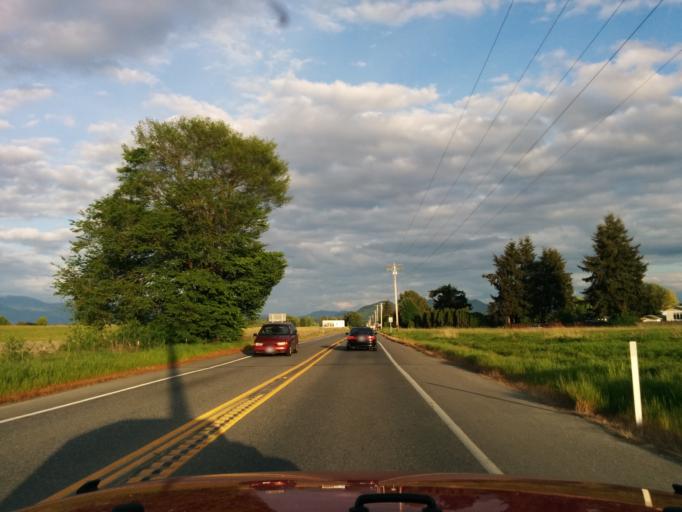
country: US
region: Washington
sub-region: Skagit County
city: Mount Vernon
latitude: 48.4356
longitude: -122.3773
